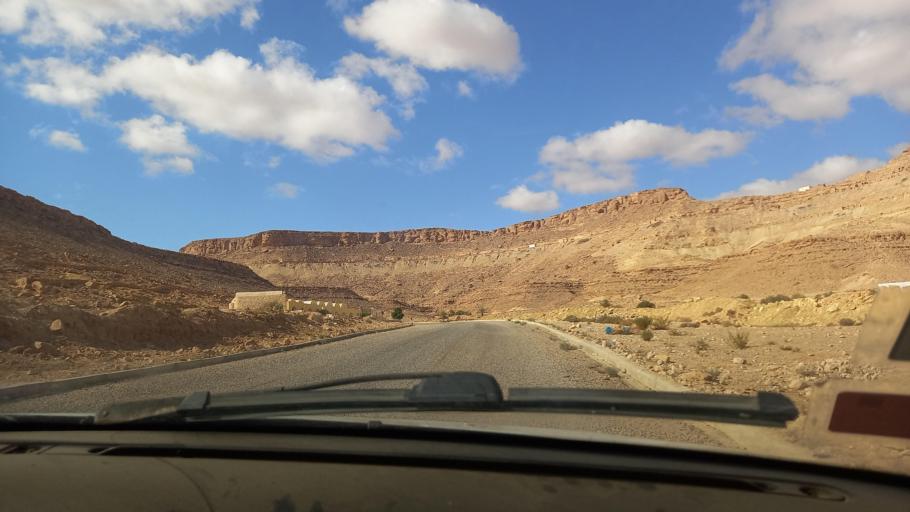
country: TN
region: Tataouine
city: Tataouine
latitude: 32.9838
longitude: 10.2602
